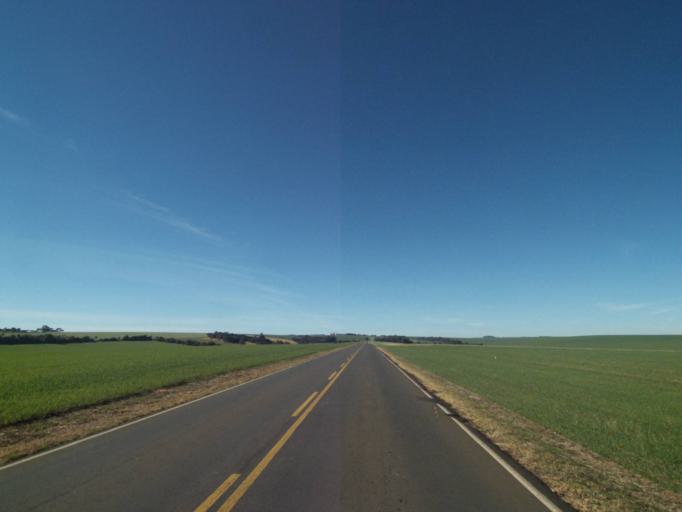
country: BR
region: Parana
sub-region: Tibagi
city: Tibagi
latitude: -24.5238
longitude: -50.3263
